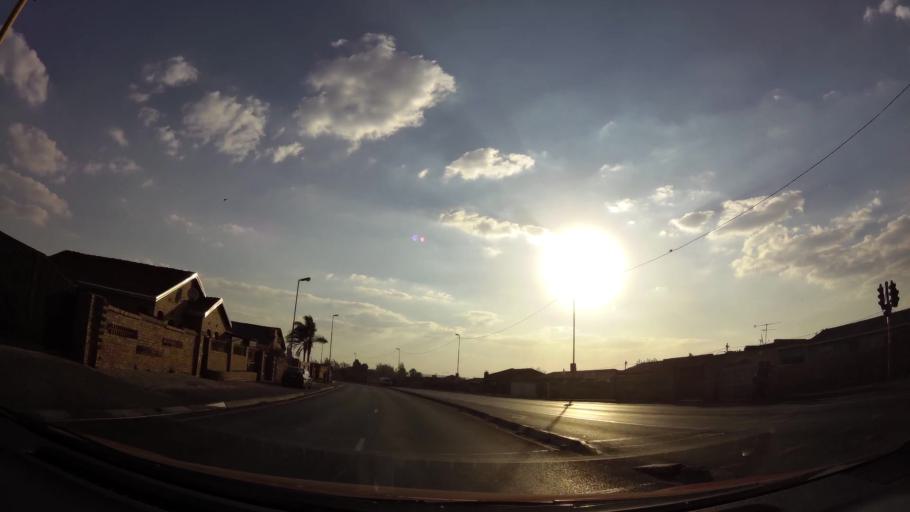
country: ZA
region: Gauteng
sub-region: City of Johannesburg Metropolitan Municipality
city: Roodepoort
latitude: -26.2125
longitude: 27.8946
